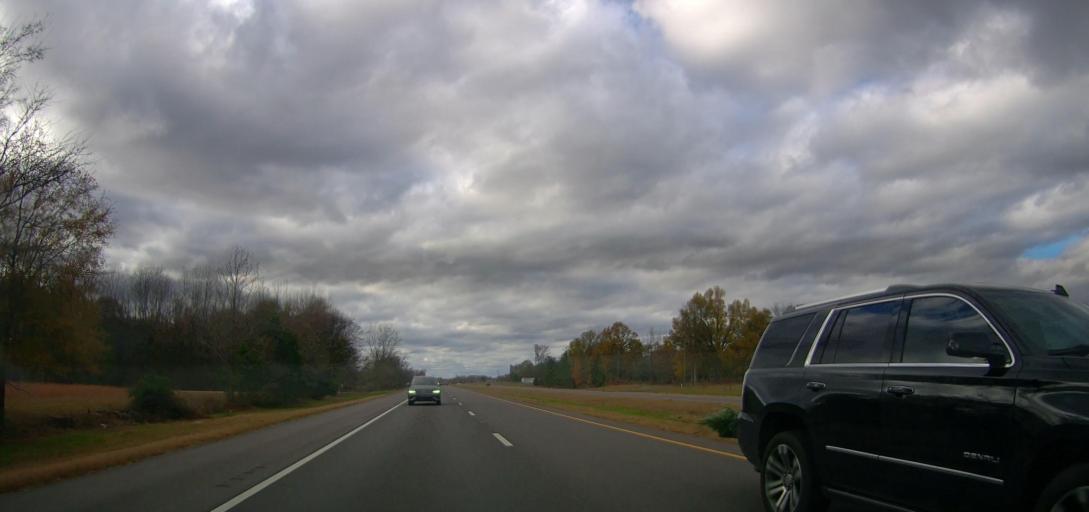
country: US
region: Alabama
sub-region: Lawrence County
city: Moulton
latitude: 34.4598
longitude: -87.2429
